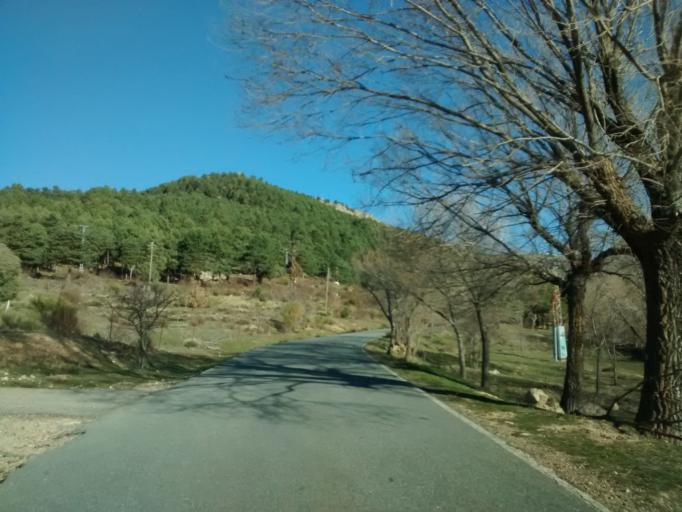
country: ES
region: Madrid
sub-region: Provincia de Madrid
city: Navacerrada
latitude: 40.7409
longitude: -4.0040
